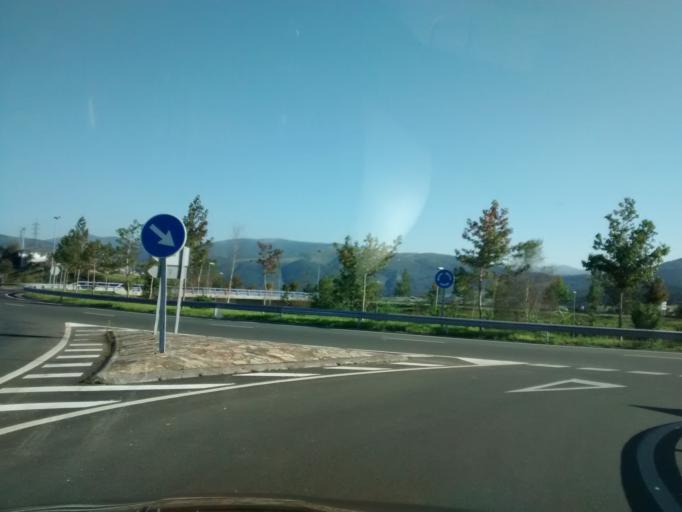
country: ES
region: Cantabria
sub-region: Provincia de Cantabria
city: Cabezon de la Sal
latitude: 43.3179
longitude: -4.2509
